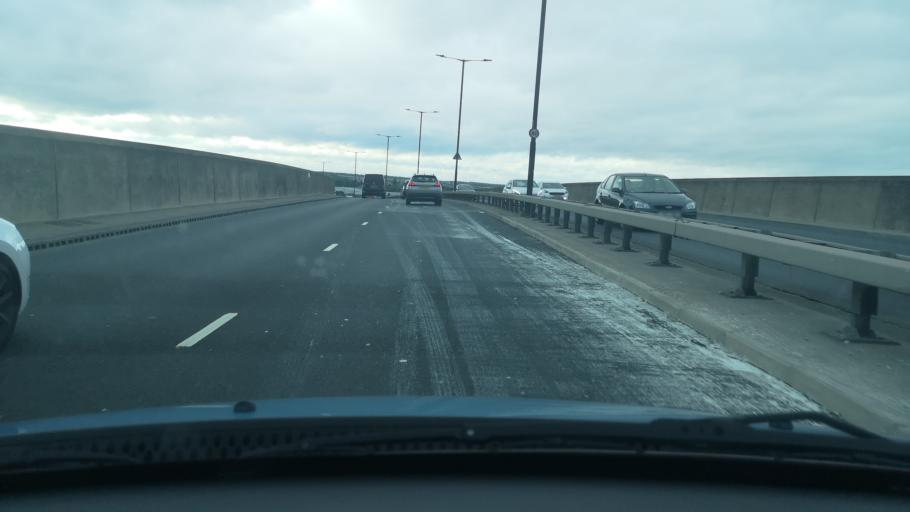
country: GB
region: England
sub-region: Doncaster
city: Doncaster
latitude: 53.5291
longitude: -1.1388
